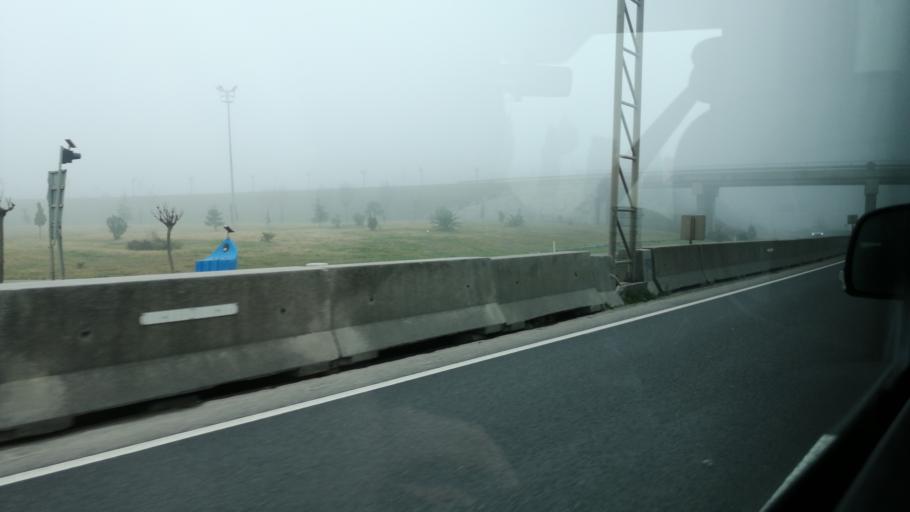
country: TR
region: Yalova
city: Taskopru
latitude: 40.6820
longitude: 29.3619
